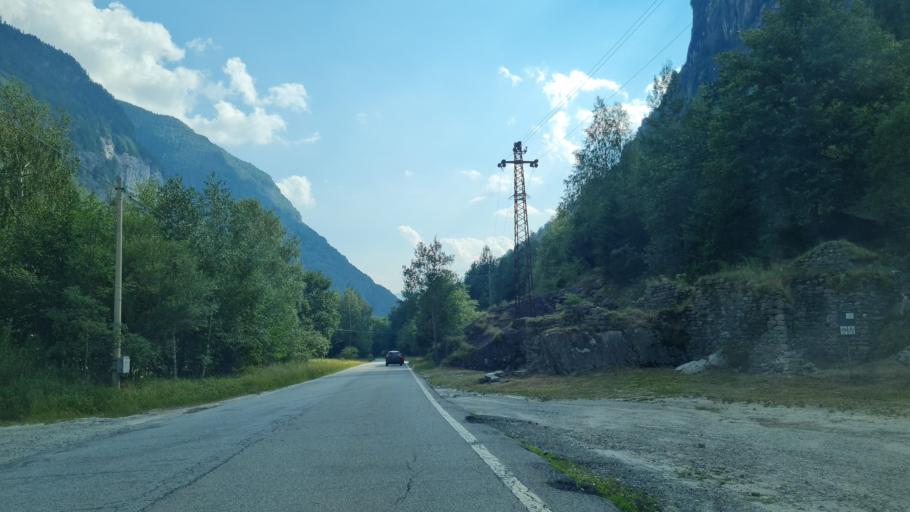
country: IT
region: Piedmont
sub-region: Provincia Verbano-Cusio-Ossola
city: Premia
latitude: 46.3181
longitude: 8.3831
